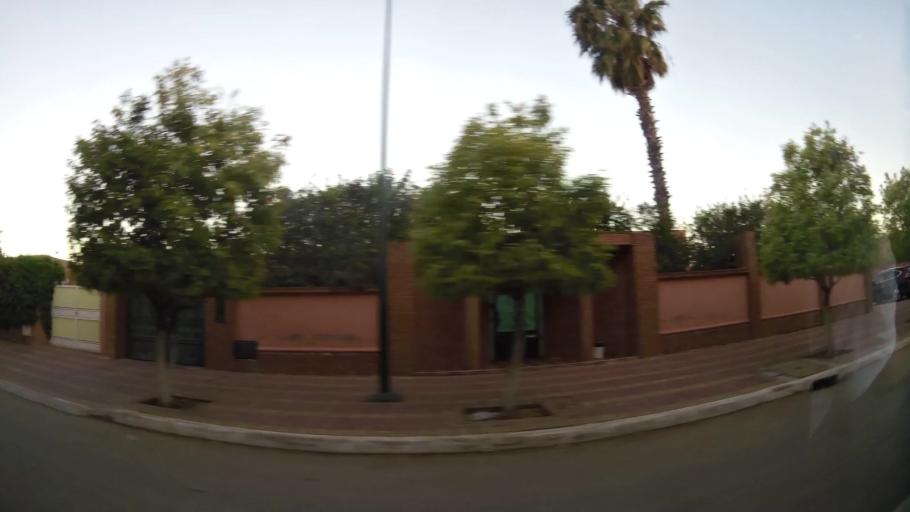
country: MA
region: Marrakech-Tensift-Al Haouz
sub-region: Kelaa-Des-Sraghna
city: Sidi Bou Othmane
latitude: 32.2116
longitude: -7.9314
